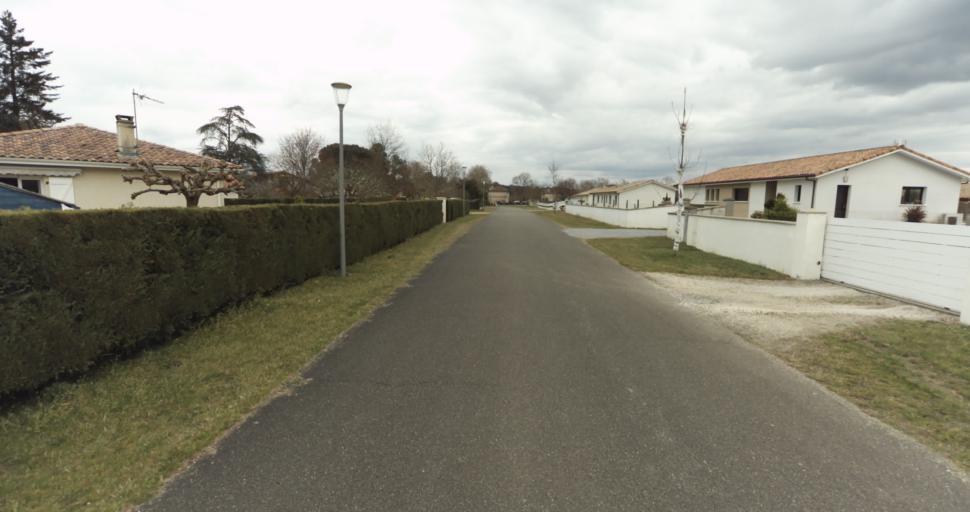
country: FR
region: Aquitaine
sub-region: Departement des Landes
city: Sarbazan
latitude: 44.0209
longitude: -0.3141
